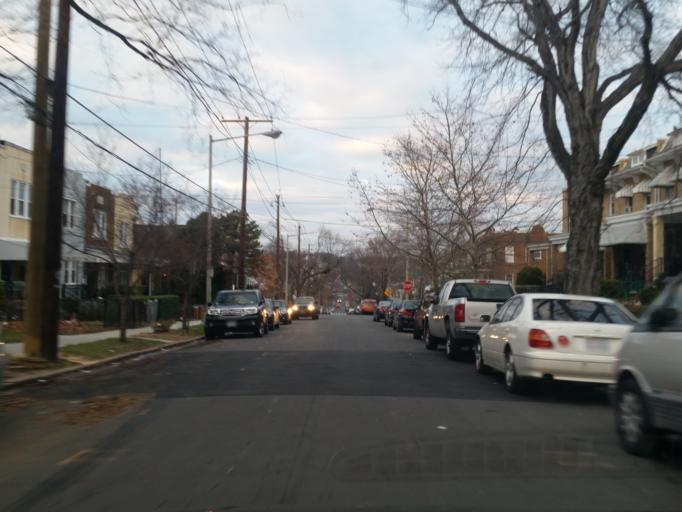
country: US
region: Maryland
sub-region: Montgomery County
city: Takoma Park
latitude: 38.9504
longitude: -77.0220
